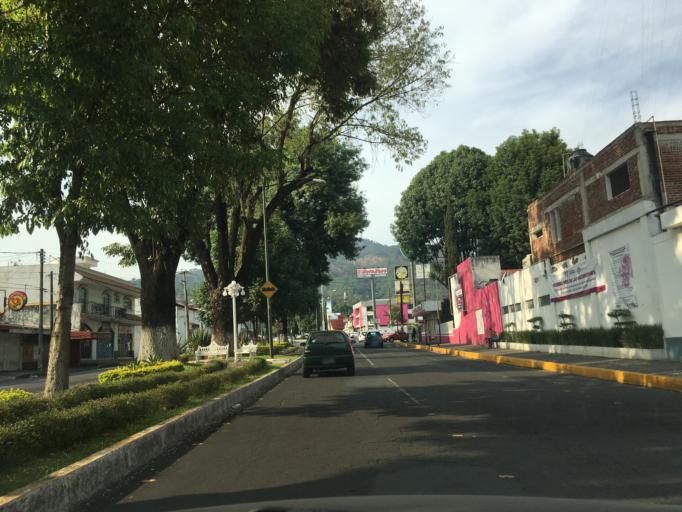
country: MX
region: Michoacan
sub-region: Uruapan
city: Uruapan
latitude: 19.4218
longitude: -102.0479
